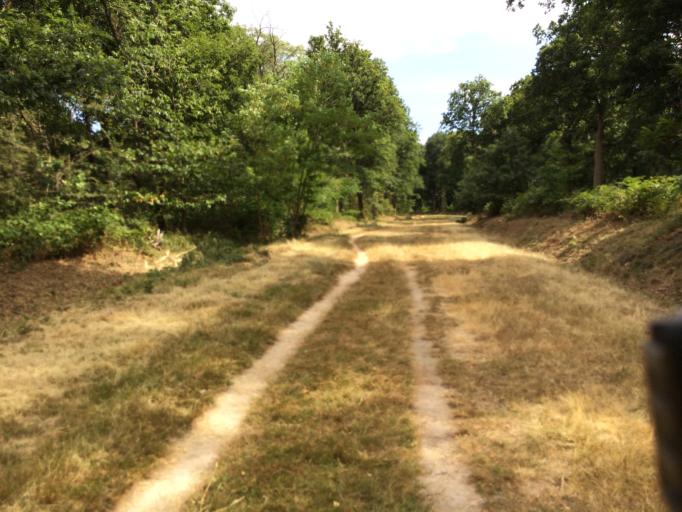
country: FR
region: Ile-de-France
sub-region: Departement de l'Essonne
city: Draveil
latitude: 48.6768
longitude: 2.4427
